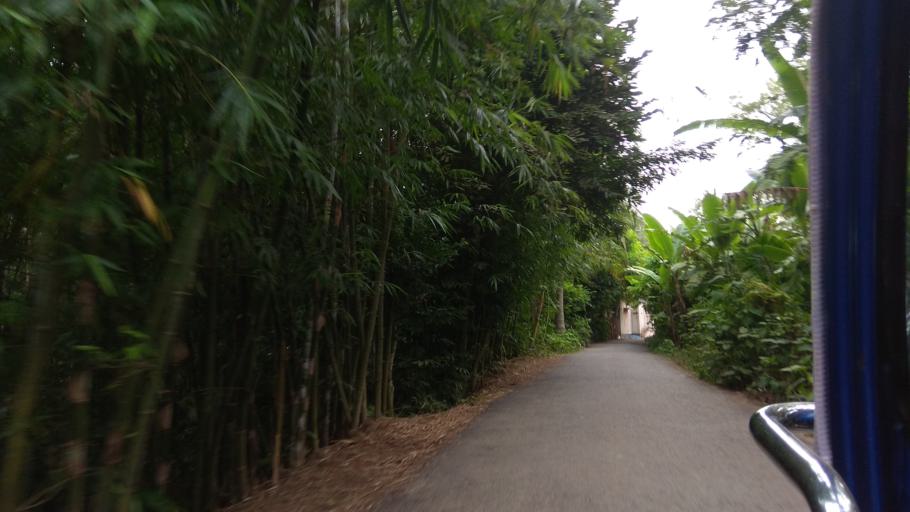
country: BD
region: Khulna
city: Kalia
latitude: 23.0321
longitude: 89.6554
